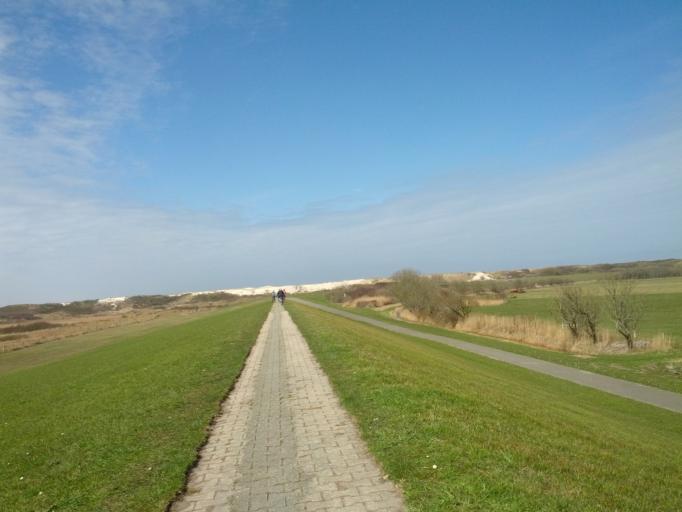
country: DE
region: Lower Saxony
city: Langeoog
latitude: 53.7310
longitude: 7.4739
